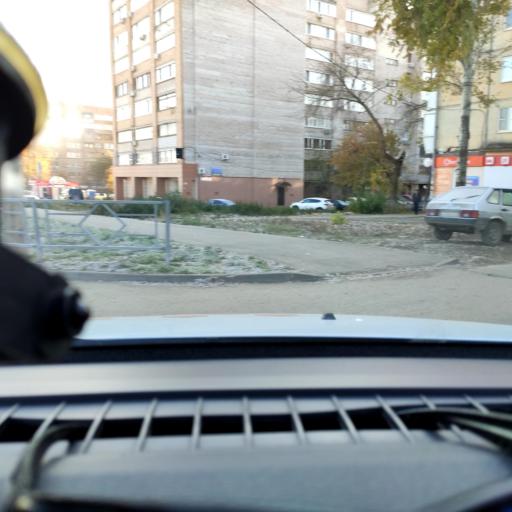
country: RU
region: Samara
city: Samara
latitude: 53.1971
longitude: 50.1979
